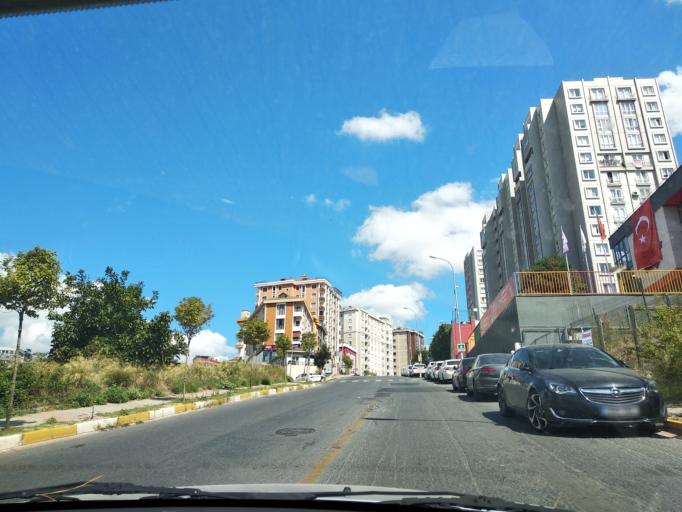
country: TR
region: Istanbul
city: Umraniye
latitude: 41.0080
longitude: 29.1082
